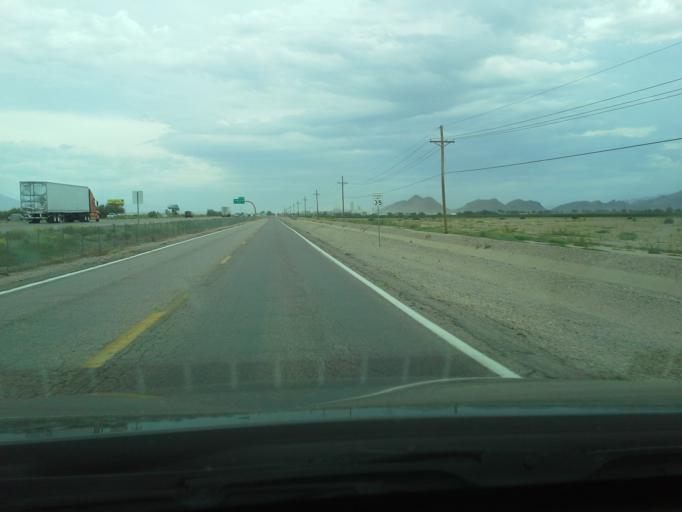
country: US
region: Arizona
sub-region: Pima County
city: Marana
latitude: 32.4341
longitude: -111.1778
